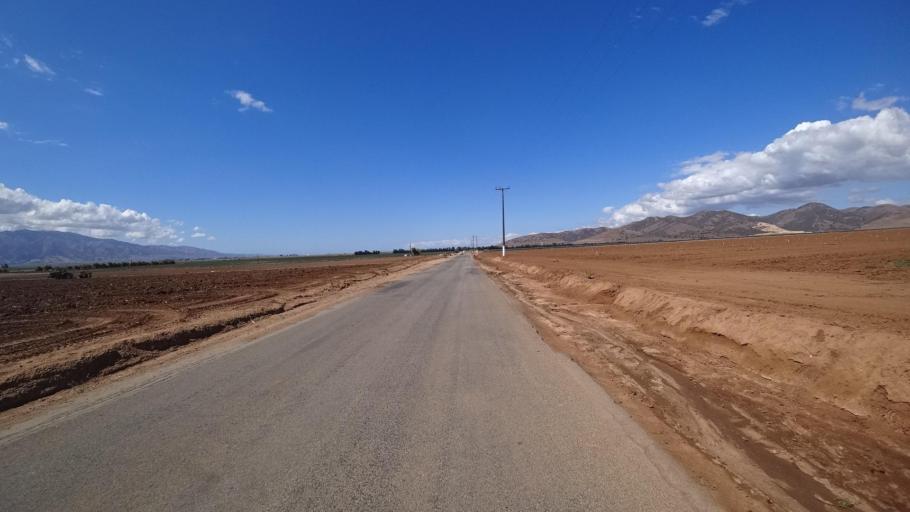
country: US
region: California
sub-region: Monterey County
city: Gonzales
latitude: 36.5438
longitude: -121.4321
